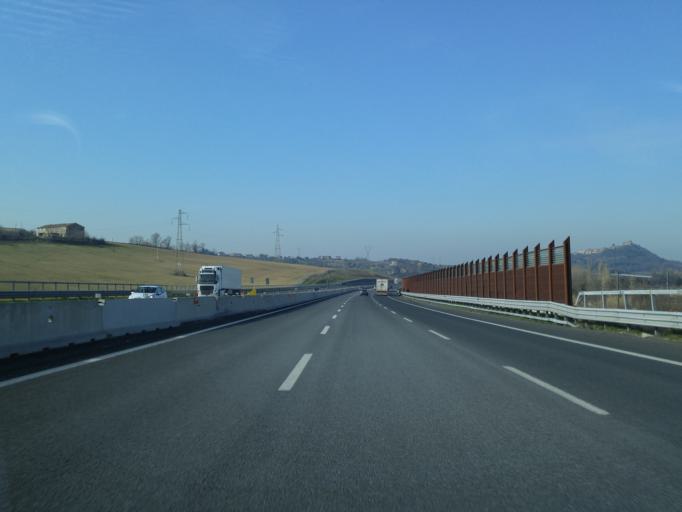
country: IT
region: The Marches
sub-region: Provincia di Pesaro e Urbino
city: Gradara
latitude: 43.9264
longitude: 12.8018
